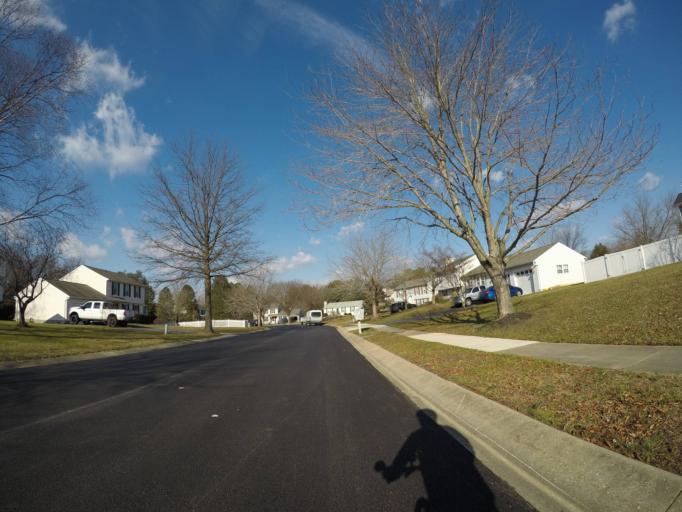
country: US
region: Maryland
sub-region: Howard County
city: Ilchester
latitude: 39.2168
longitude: -76.7925
